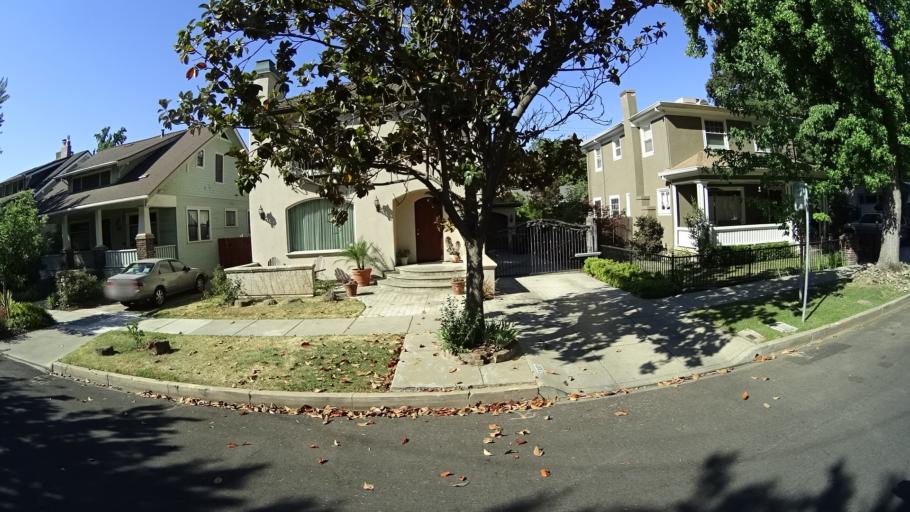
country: US
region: California
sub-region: Sacramento County
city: Sacramento
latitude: 38.5511
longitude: -121.4846
